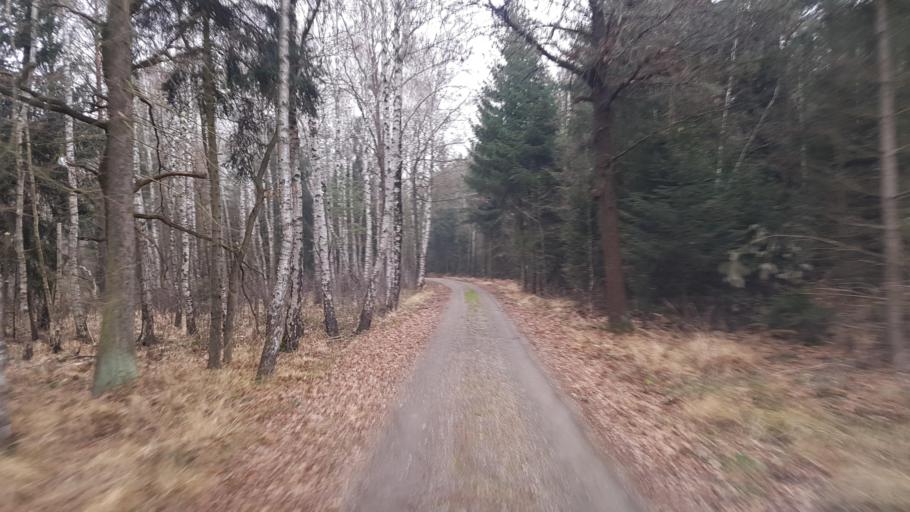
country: DE
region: Brandenburg
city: Plessa
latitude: 51.5192
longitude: 13.6304
